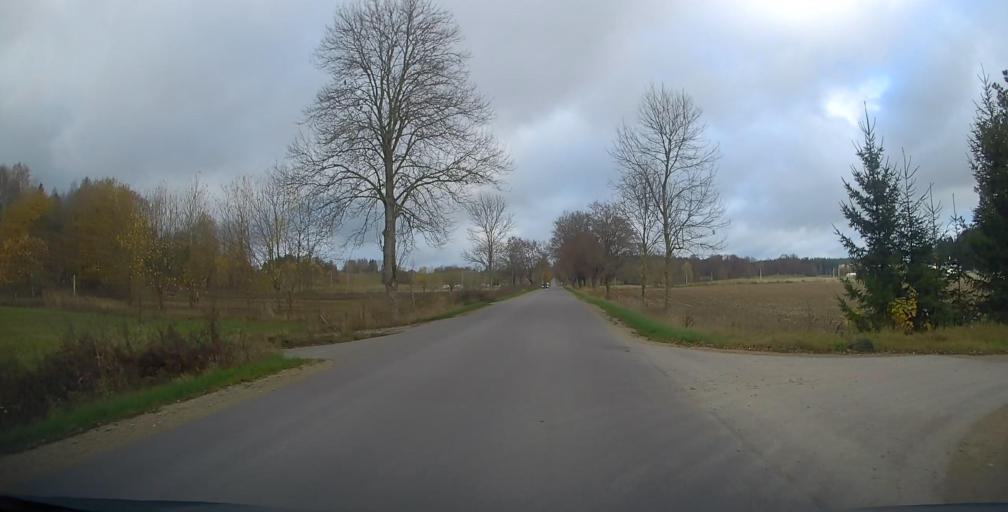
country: PL
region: Podlasie
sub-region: Suwalki
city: Suwalki
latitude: 54.2996
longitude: 22.8786
